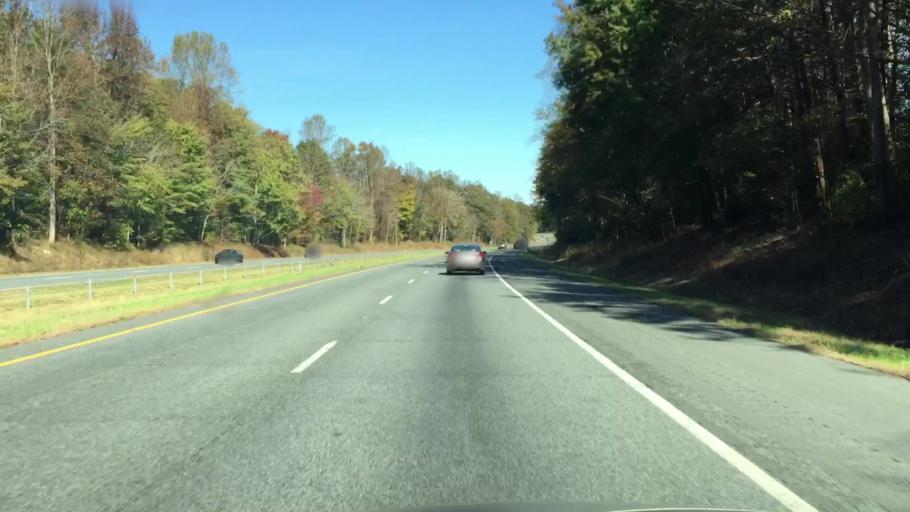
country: US
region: North Carolina
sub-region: Rockingham County
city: Reidsville
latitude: 36.2925
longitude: -79.6416
